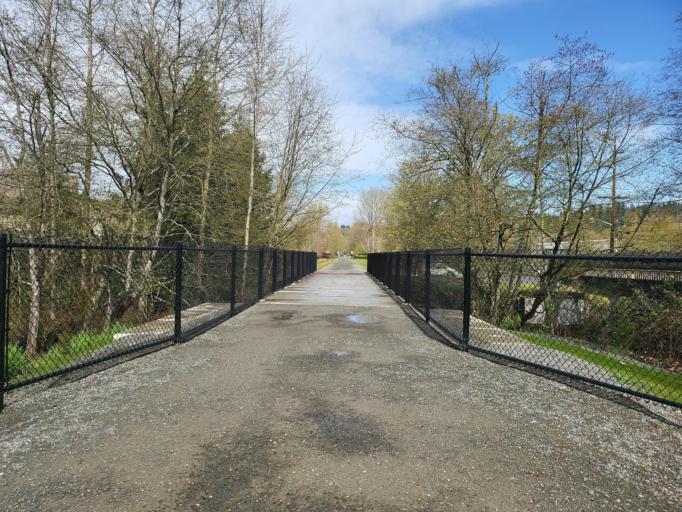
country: US
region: Washington
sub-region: King County
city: Mercer Island
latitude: 47.5299
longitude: -122.2016
